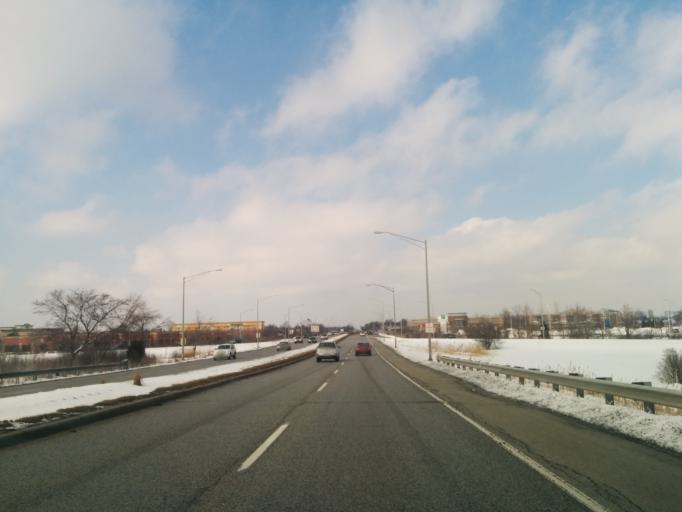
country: US
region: Illinois
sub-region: Cook County
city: Tinley Park
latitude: 41.5529
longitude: -87.7925
